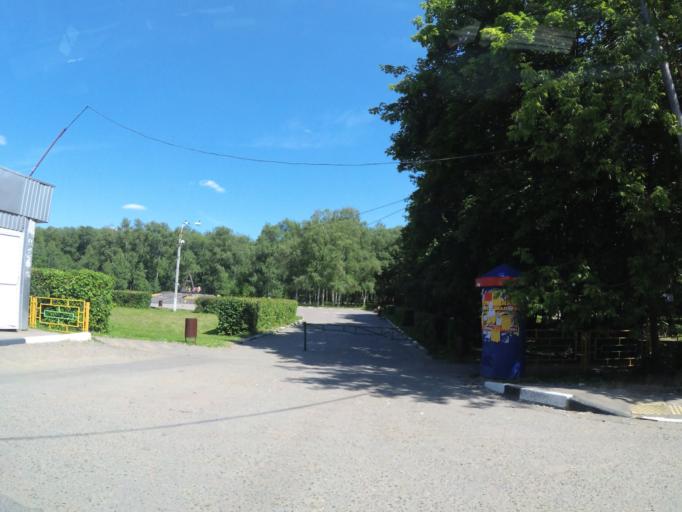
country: RU
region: Moskovskaya
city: Lobnya
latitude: 56.0131
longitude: 37.4684
